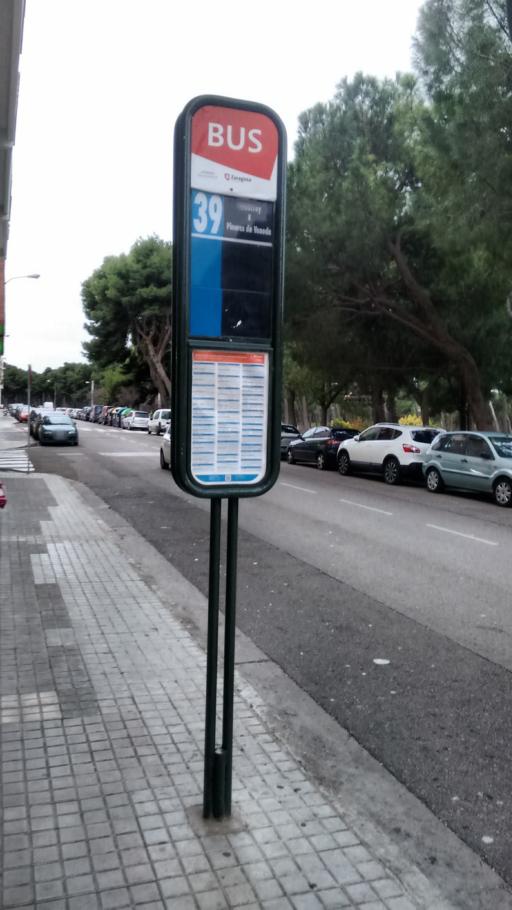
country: ES
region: Aragon
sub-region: Provincia de Zaragoza
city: Delicias
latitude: 41.6292
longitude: -0.8909
